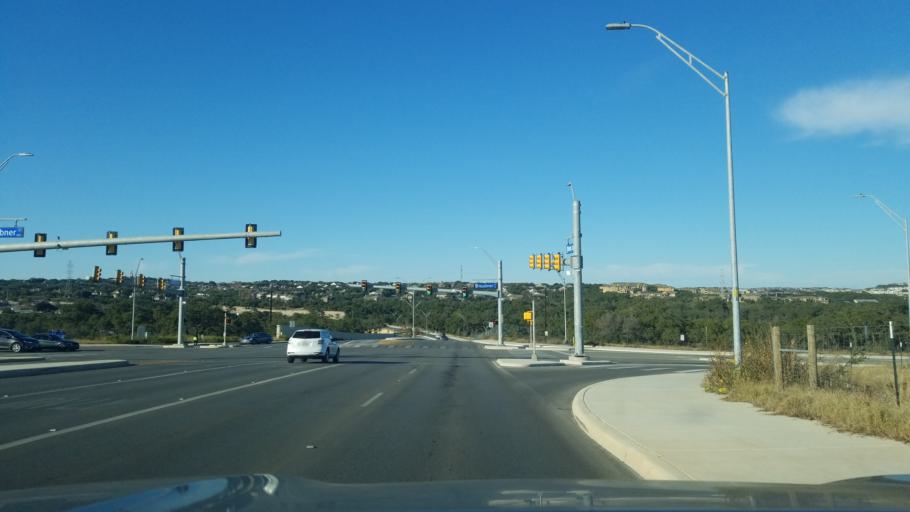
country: US
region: Texas
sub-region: Bexar County
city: Hollywood Park
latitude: 29.6245
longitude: -98.4766
